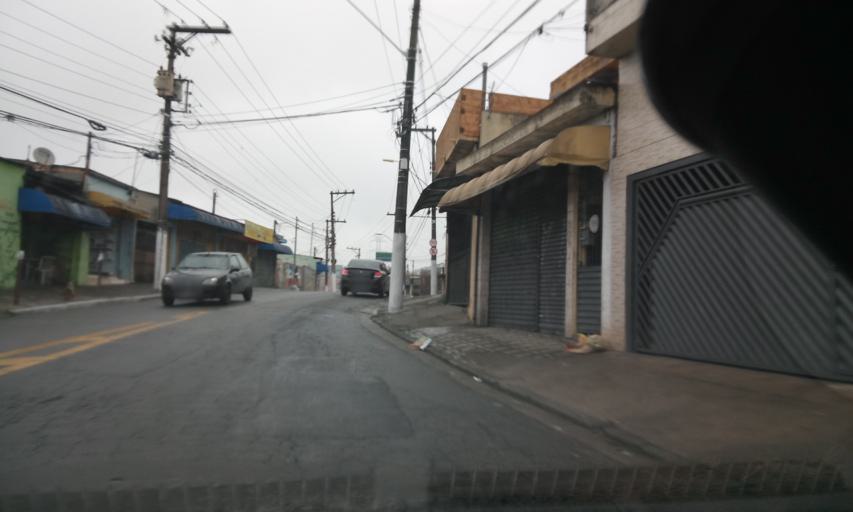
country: BR
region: Sao Paulo
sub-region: Santo Andre
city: Santo Andre
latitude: -23.7024
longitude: -46.5190
